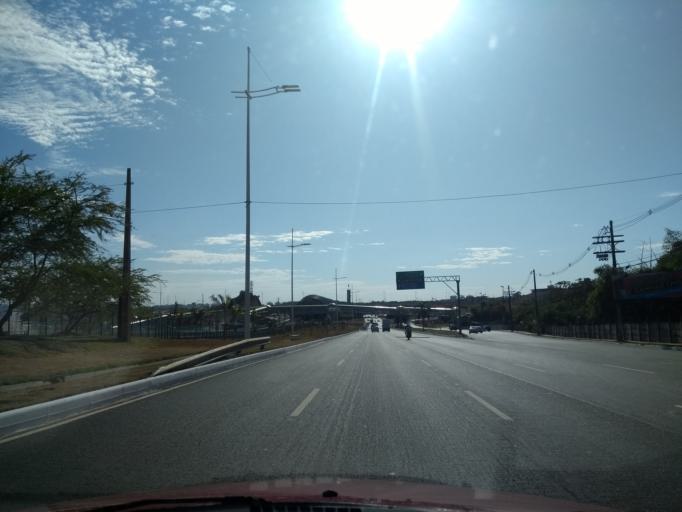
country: BR
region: Bahia
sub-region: Lauro De Freitas
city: Lauro de Freitas
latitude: -12.9247
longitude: -38.3775
